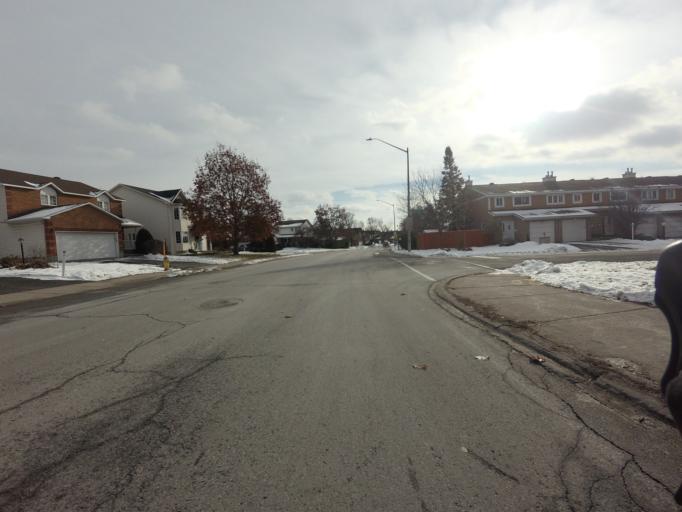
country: CA
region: Ontario
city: Bells Corners
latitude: 45.2714
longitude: -75.7658
